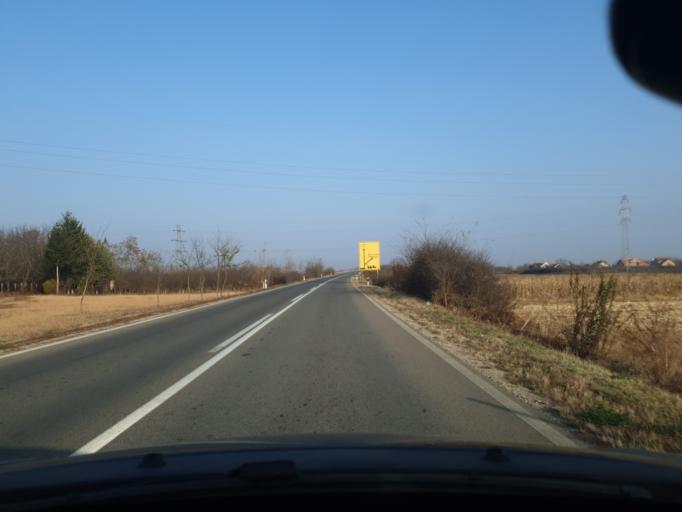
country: RS
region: Central Serbia
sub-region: Jablanicki Okrug
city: Leskovac
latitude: 42.9702
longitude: 21.9764
